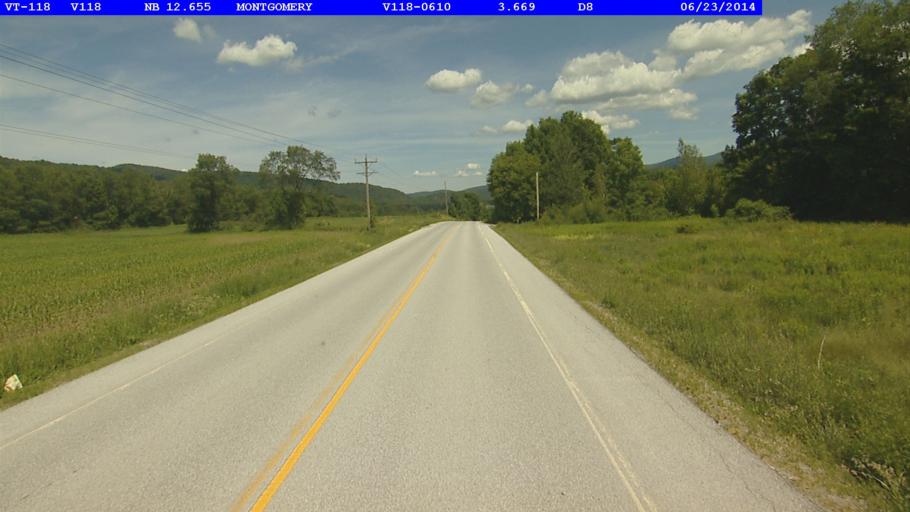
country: US
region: Vermont
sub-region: Franklin County
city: Richford
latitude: 44.8506
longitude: -72.6107
